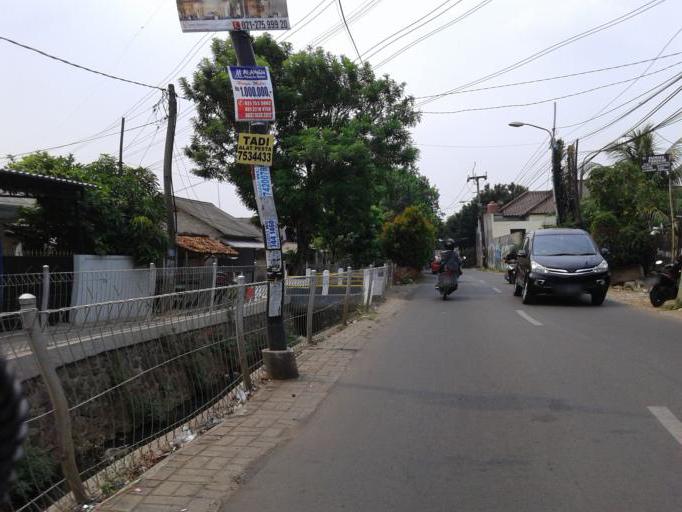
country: ID
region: West Java
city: Pamulang
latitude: -6.3186
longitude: 106.7607
